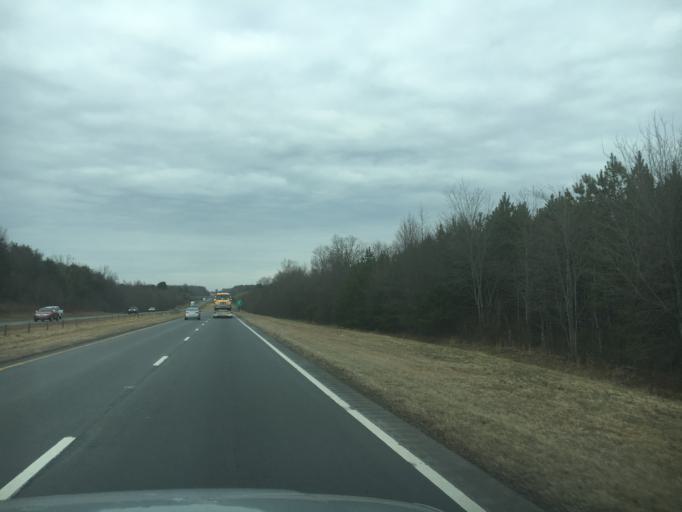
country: US
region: North Carolina
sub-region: Lincoln County
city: Lincolnton
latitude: 35.5075
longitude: -81.2238
